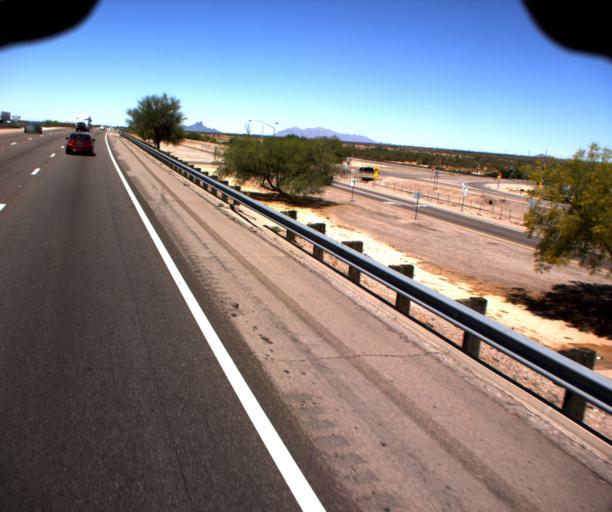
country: US
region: Arizona
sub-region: Pima County
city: Marana
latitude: 32.4612
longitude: -111.2153
